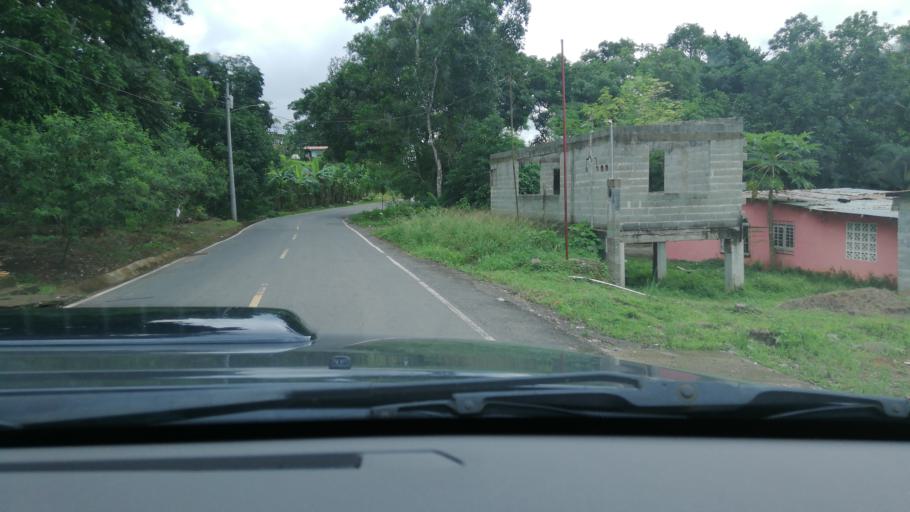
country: PA
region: Panama
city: Cerro Azul
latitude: 9.1113
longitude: -79.4433
